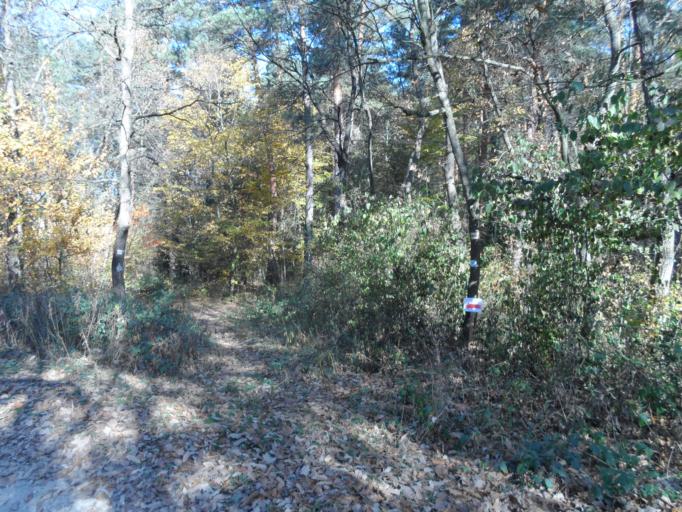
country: HU
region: Veszprem
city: Ajka
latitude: 47.2157
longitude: 17.5633
